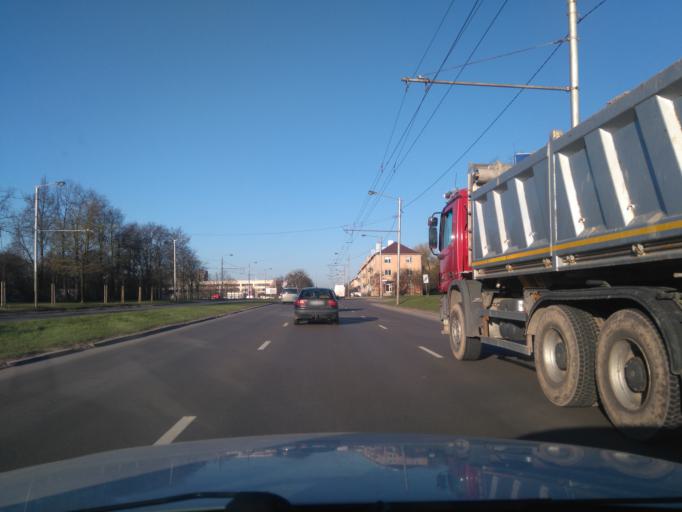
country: LT
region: Kauno apskritis
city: Dainava (Kaunas)
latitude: 54.8990
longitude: 23.9609
